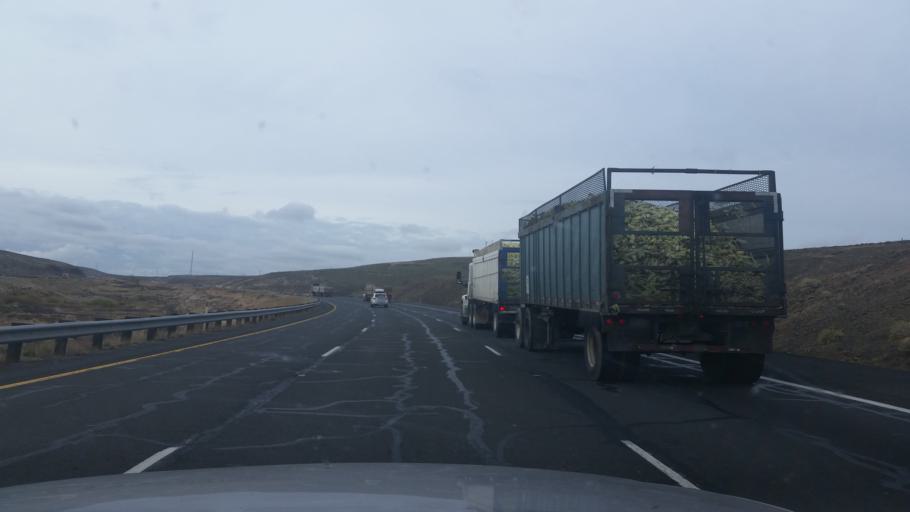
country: US
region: Washington
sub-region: Grant County
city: Mattawa
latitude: 46.9388
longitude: -120.0483
